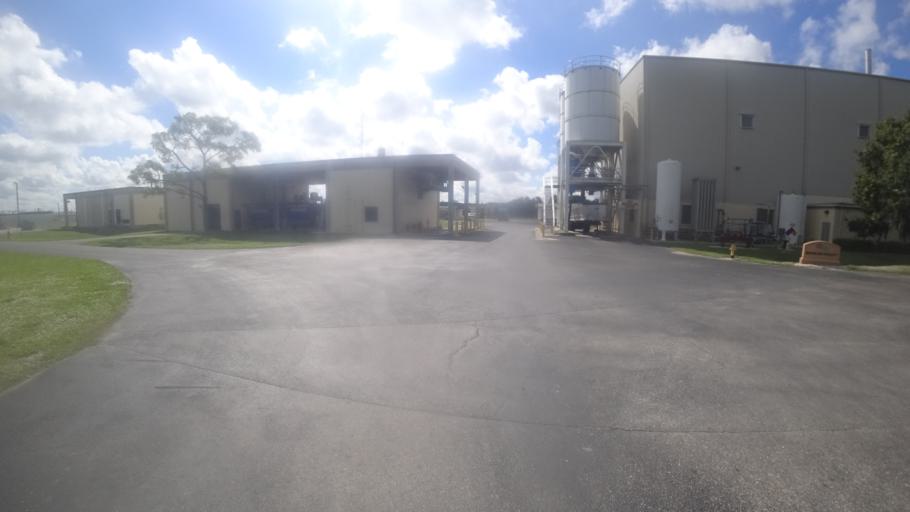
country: US
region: Florida
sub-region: Manatee County
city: Samoset
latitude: 27.4688
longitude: -82.4516
